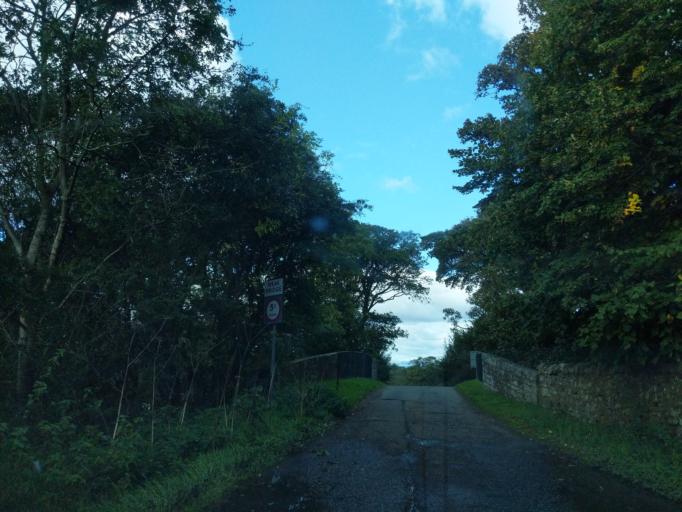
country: GB
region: Scotland
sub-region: Edinburgh
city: Currie
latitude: 55.9185
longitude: -3.3239
